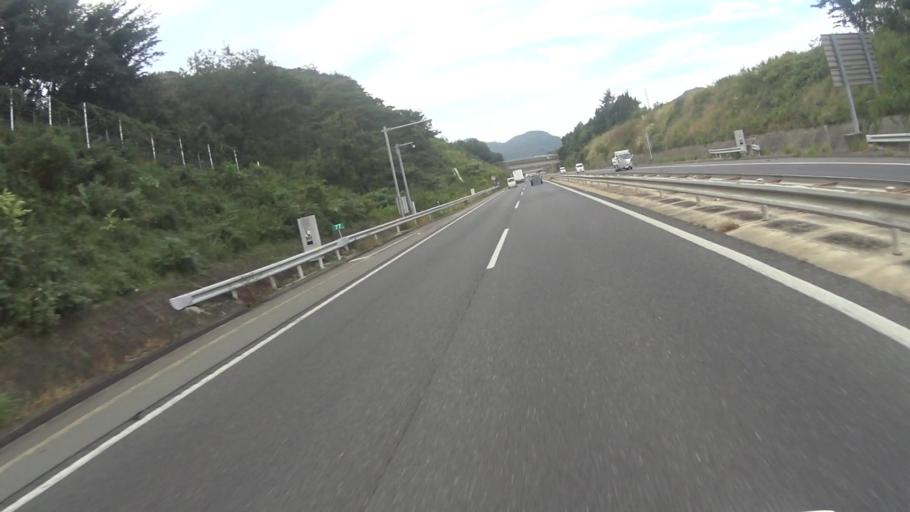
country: JP
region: Kyoto
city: Kameoka
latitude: 34.9898
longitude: 135.5940
